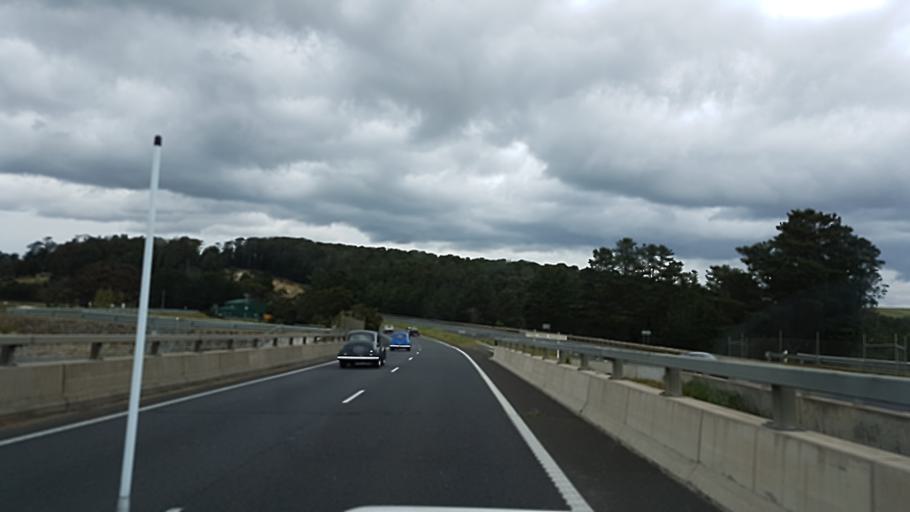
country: AU
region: Victoria
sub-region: Moorabool
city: Bacchus Marsh
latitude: -37.6106
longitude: 144.2951
